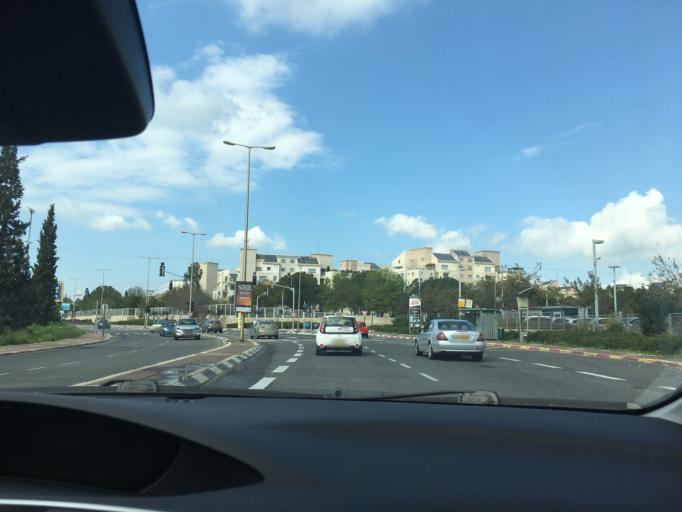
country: IL
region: Central District
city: Jaljulya
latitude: 32.1761
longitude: 34.9356
